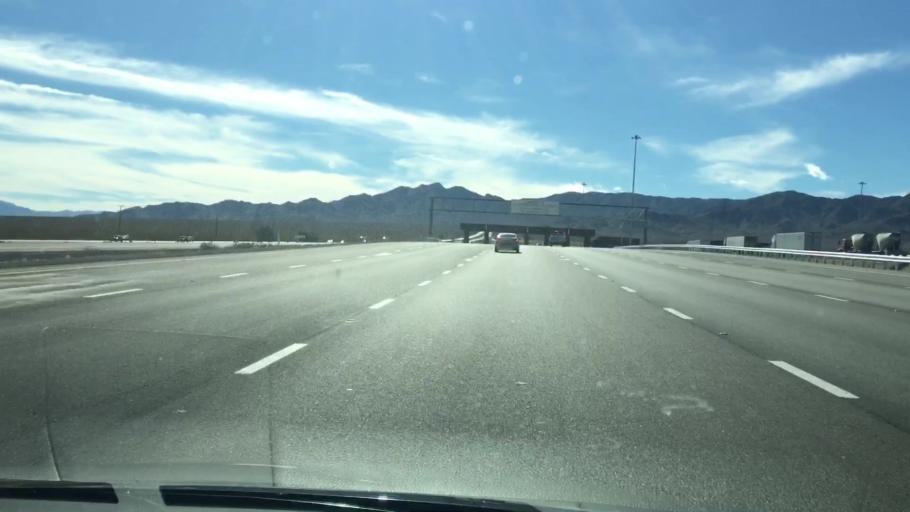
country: US
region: Nevada
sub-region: Clark County
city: Sandy Valley
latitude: 35.5184
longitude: -115.4303
